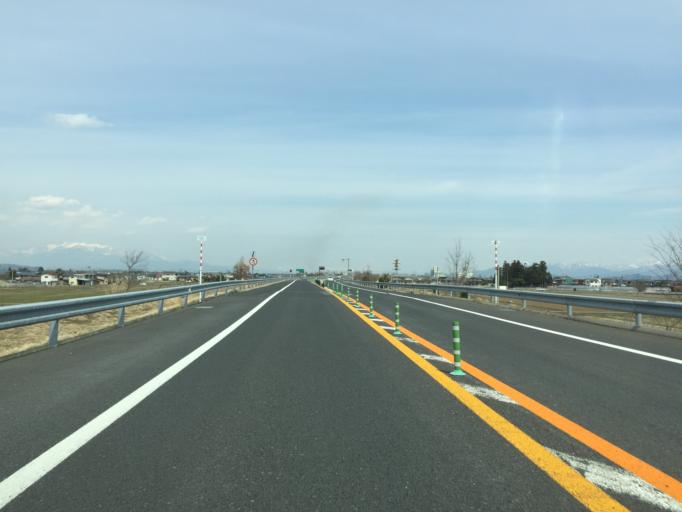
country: JP
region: Yamagata
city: Yamagata-shi
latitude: 38.2621
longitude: 140.2902
